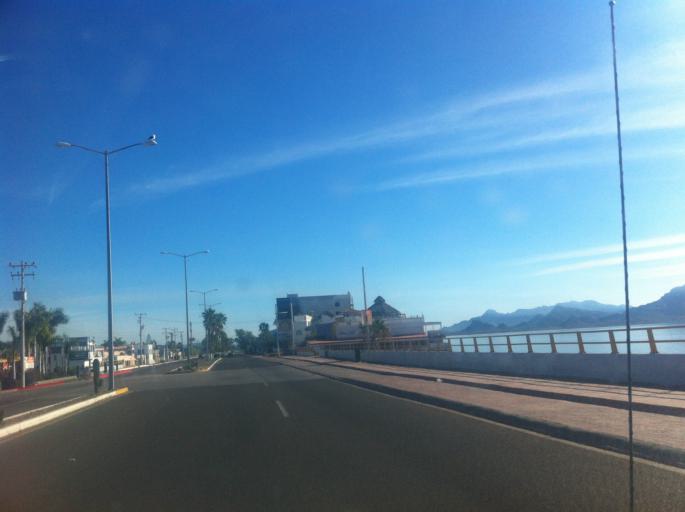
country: MX
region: Sonora
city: Heroica Guaymas
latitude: 27.9625
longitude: -111.0262
